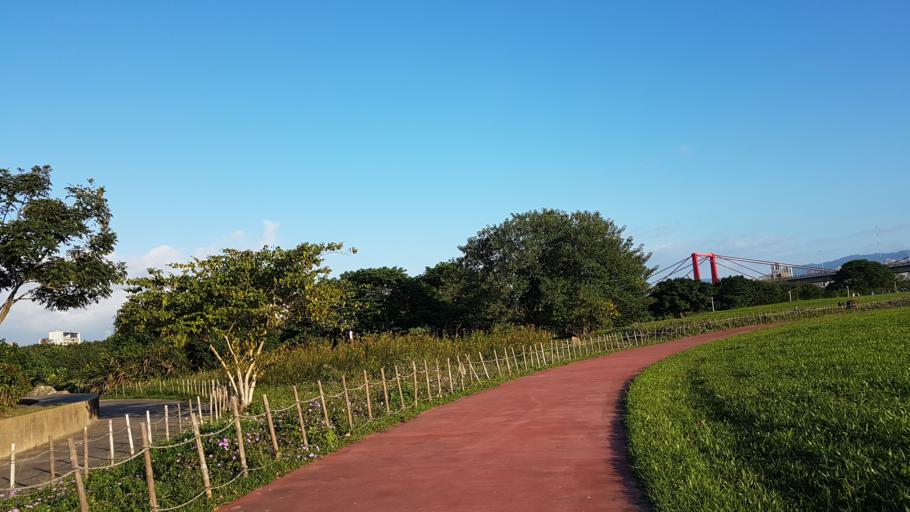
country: TW
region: Taipei
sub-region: Taipei
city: Banqiao
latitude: 25.0256
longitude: 121.4859
